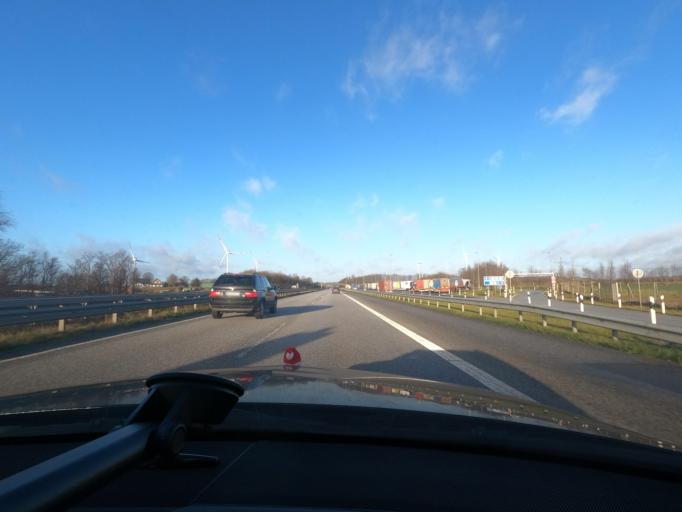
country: DE
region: Schleswig-Holstein
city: Bollingstedt
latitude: 54.6336
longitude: 9.4397
